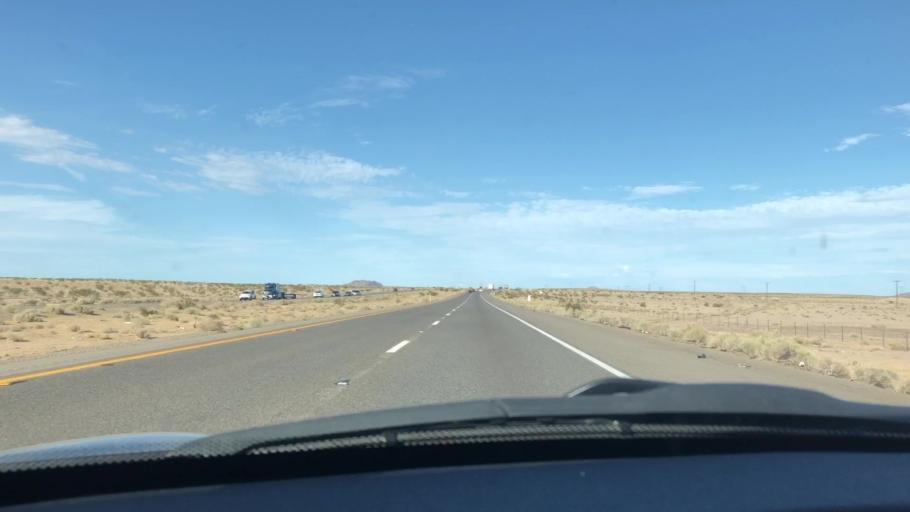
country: US
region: California
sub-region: San Bernardino County
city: Fort Irwin
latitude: 34.9988
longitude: -116.5637
